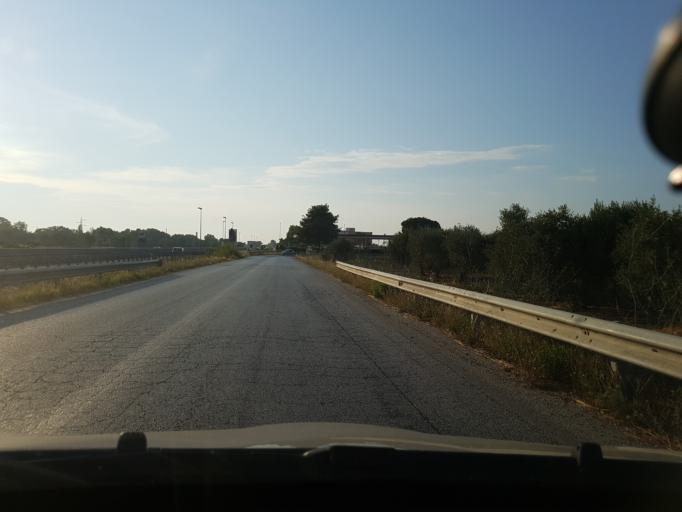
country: IT
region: Apulia
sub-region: Provincia di Foggia
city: Carapelle
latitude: 41.3964
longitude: 15.6582
